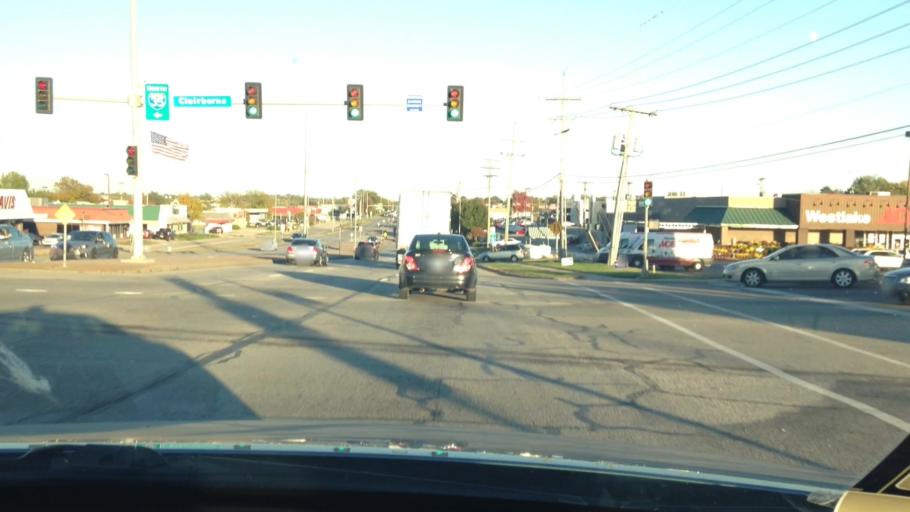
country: US
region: Kansas
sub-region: Johnson County
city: Olathe
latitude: 38.8836
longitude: -94.7892
